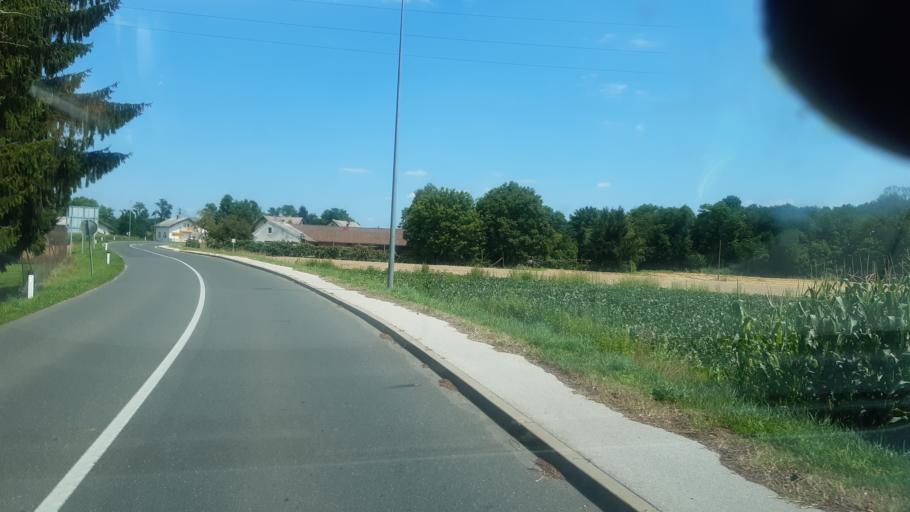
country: SI
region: Murska Sobota
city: Murska Sobota
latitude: 46.6850
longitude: 16.1833
